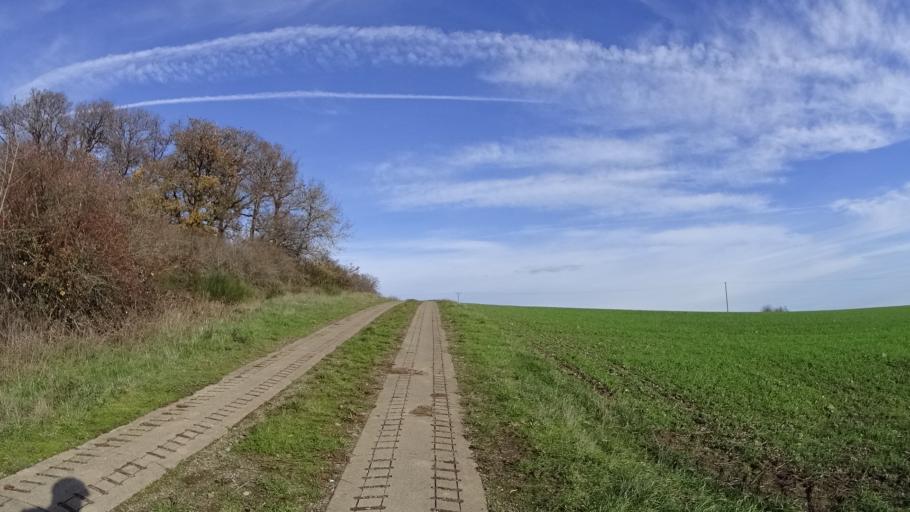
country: DE
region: Rheinland-Pfalz
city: Kirrweiler
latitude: 49.6401
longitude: 7.4930
